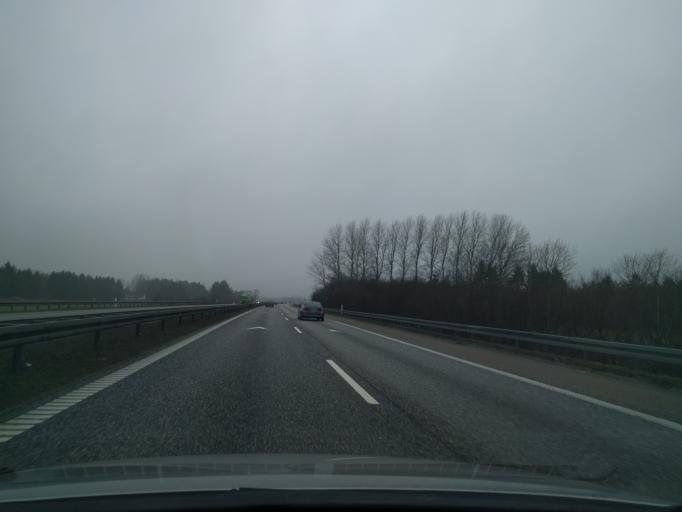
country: DK
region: Zealand
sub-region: Soro Kommune
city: Frederiksberg
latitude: 55.4502
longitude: 11.6444
